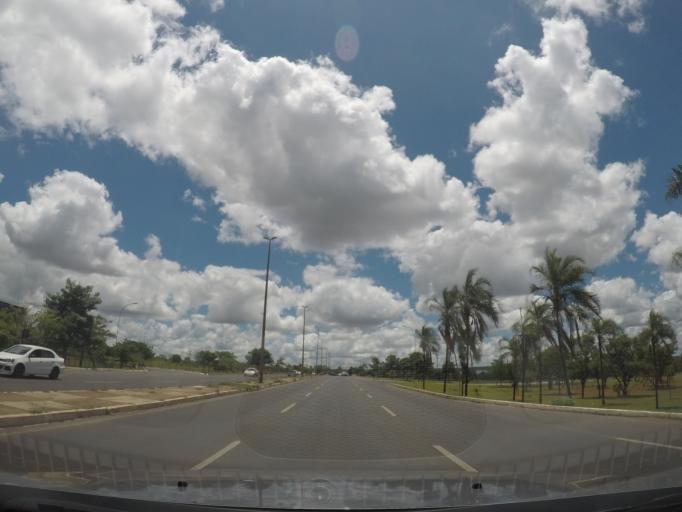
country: BR
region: Federal District
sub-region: Brasilia
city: Brasilia
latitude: -15.8106
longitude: -47.8466
